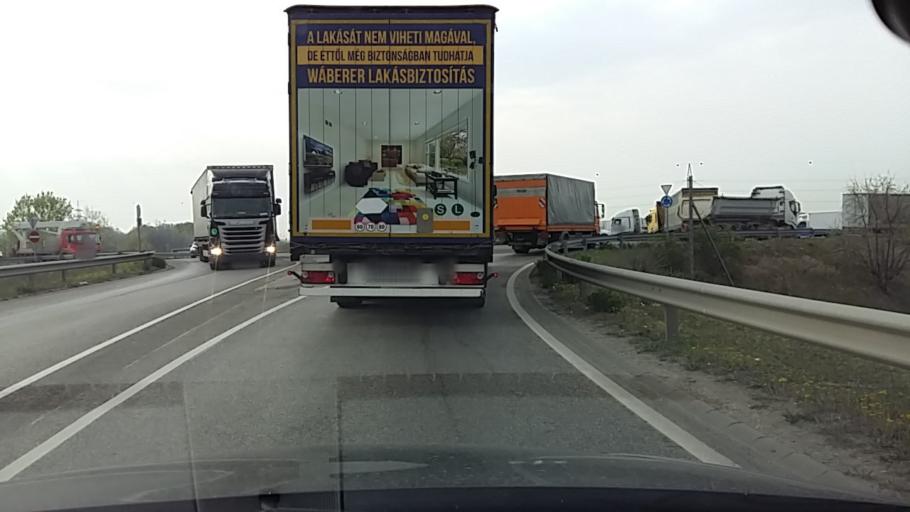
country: HU
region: Pest
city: Dunaharaszti
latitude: 47.3702
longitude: 19.1173
